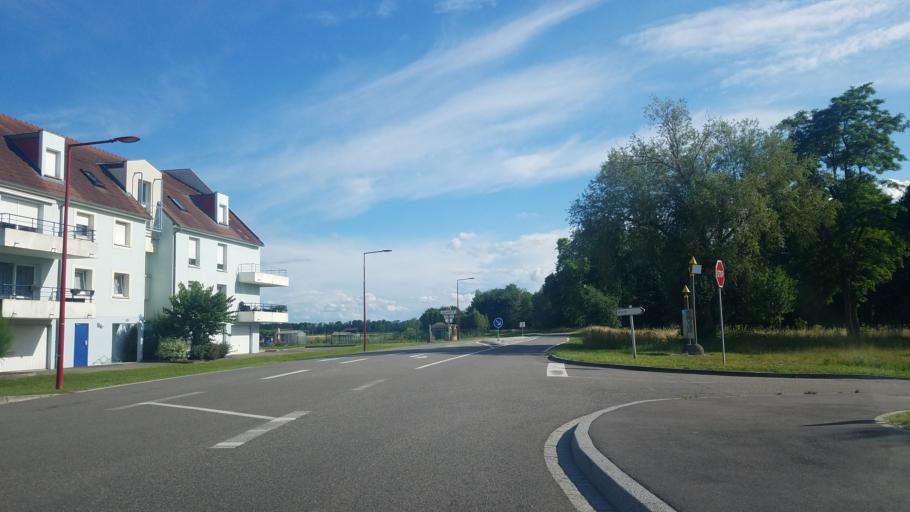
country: FR
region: Alsace
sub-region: Departement du Bas-Rhin
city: Soufflenheim
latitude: 48.8131
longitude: 7.9580
